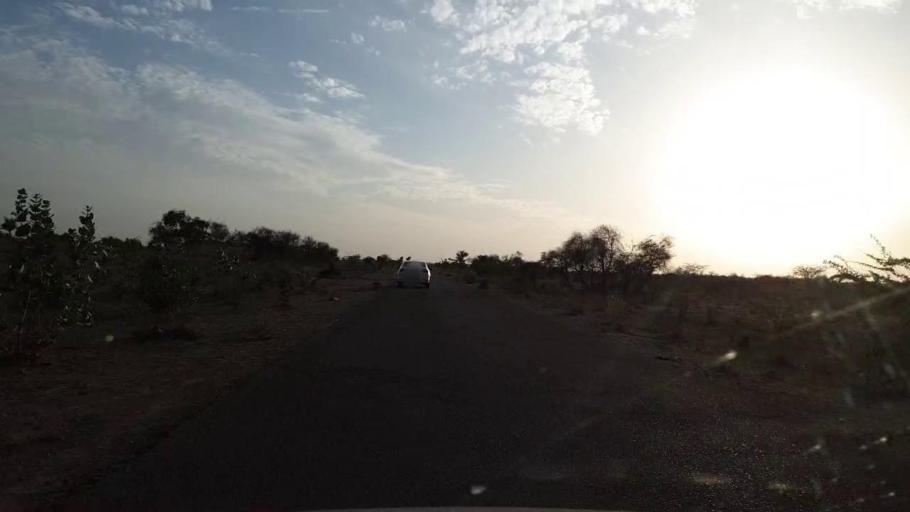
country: PK
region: Sindh
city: Nabisar
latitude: 25.0779
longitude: 69.9795
